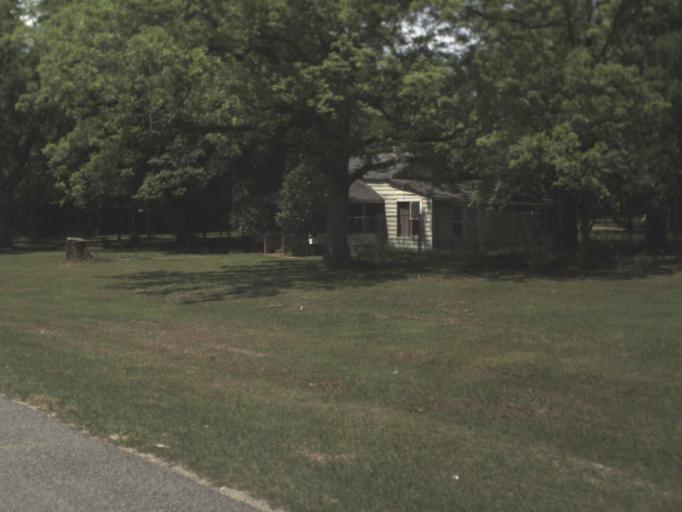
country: US
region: Florida
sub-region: Jackson County
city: Marianna
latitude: 30.5927
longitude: -85.1817
